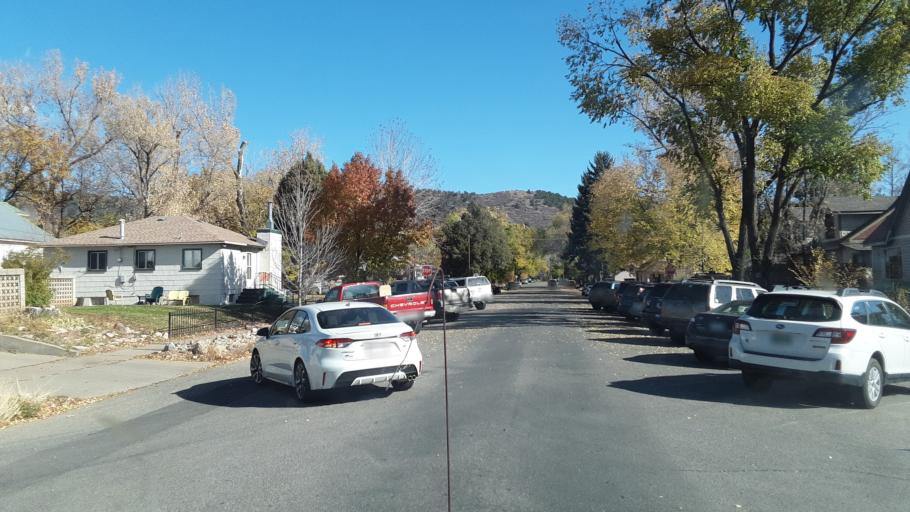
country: US
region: Colorado
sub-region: La Plata County
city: Durango
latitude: 37.2687
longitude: -107.8802
